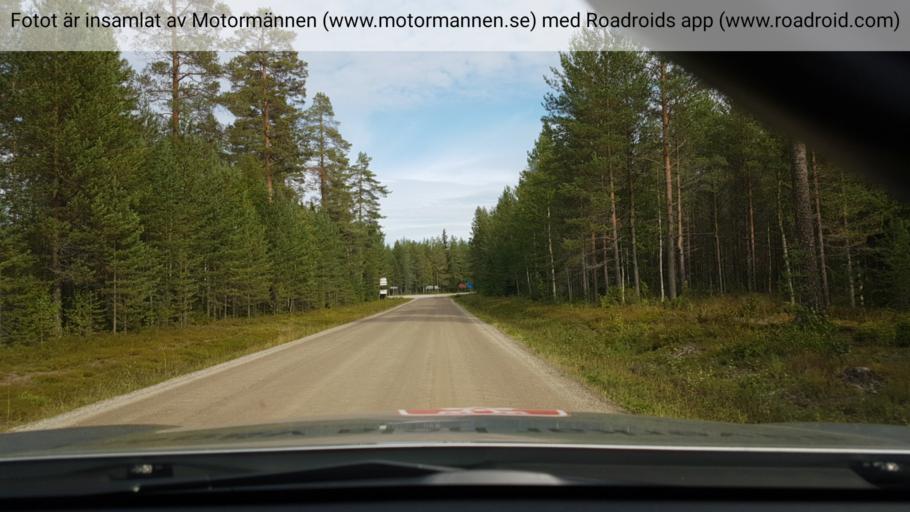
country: SE
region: Vaesterbotten
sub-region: Vindelns Kommun
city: Vindeln
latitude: 64.0831
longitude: 19.6241
